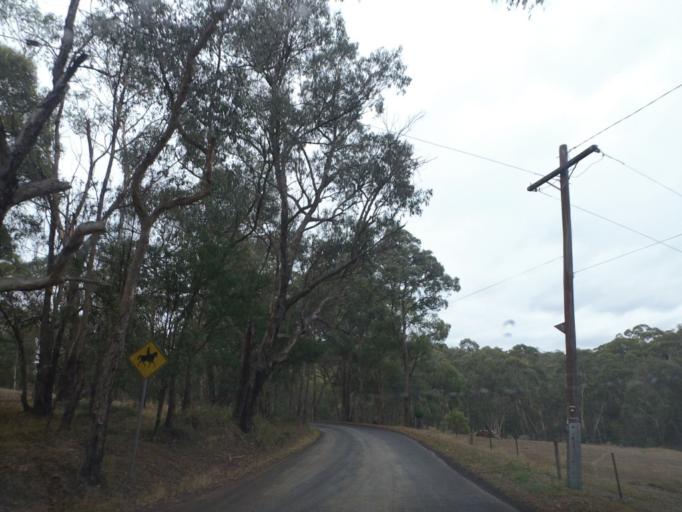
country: AU
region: Victoria
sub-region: Nillumbik
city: Saint Andrews
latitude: -37.6199
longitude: 145.2840
